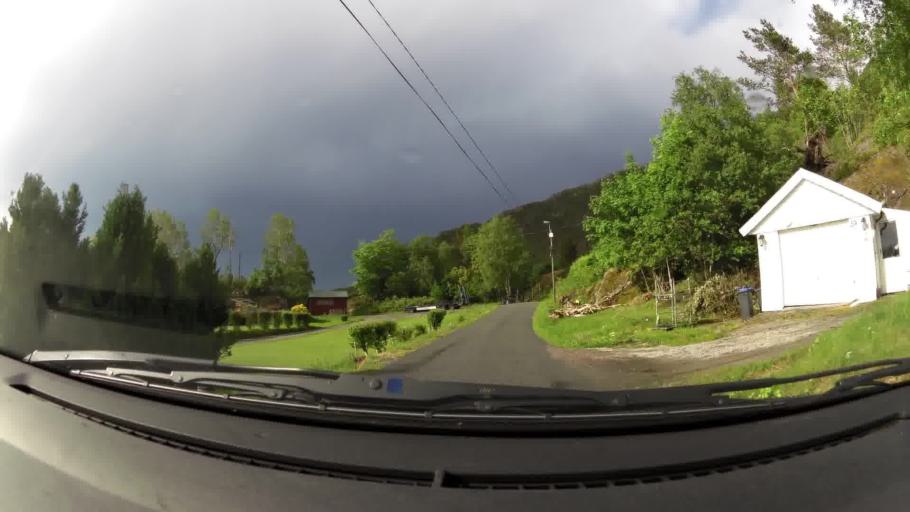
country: NO
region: More og Romsdal
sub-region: Kristiansund
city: Kristiansund
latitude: 63.0489
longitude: 7.7239
